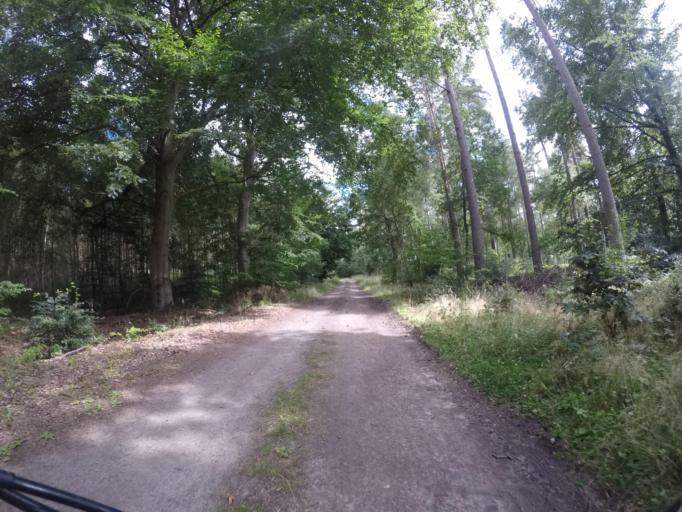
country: DE
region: Mecklenburg-Vorpommern
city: Lubtheen
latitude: 53.2642
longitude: 10.9914
